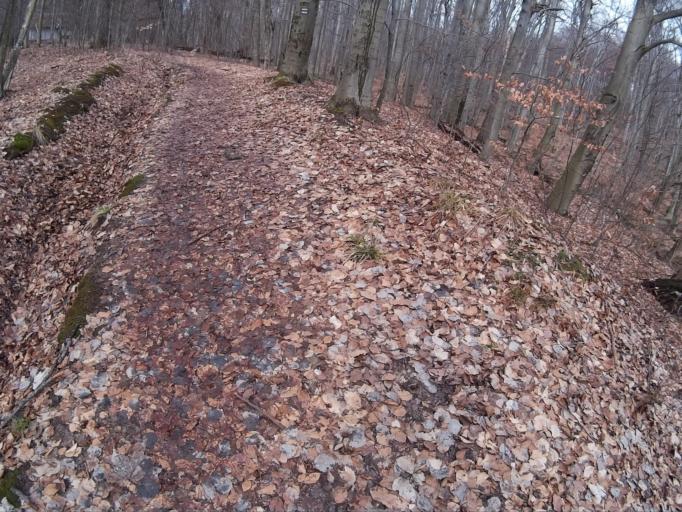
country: HU
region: Borsod-Abauj-Zemplen
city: Gonc
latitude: 48.4081
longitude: 21.4017
